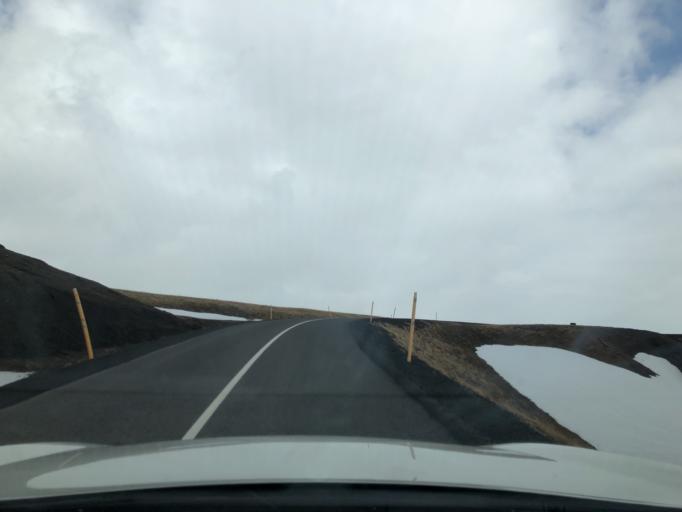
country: IS
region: Northeast
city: Laugar
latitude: 65.7107
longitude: -16.7734
